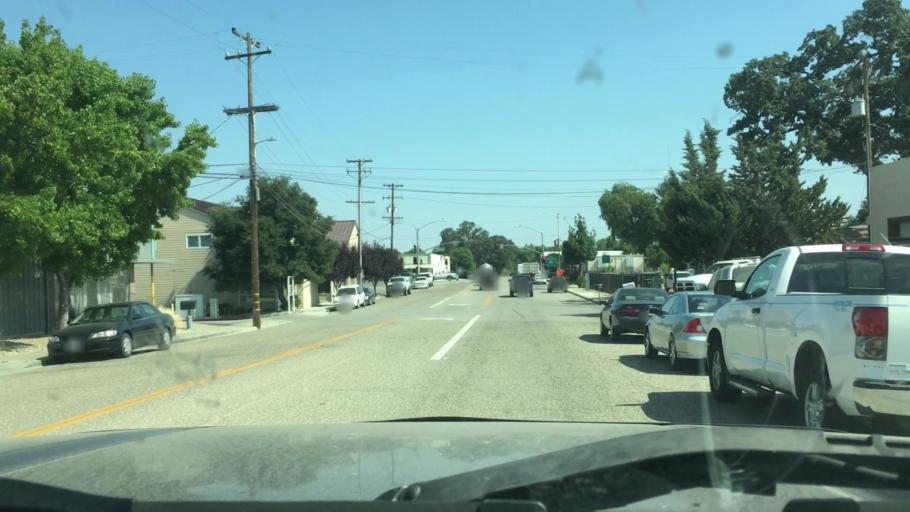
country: US
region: California
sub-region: San Luis Obispo County
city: Paso Robles
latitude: 35.6266
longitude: -120.6856
